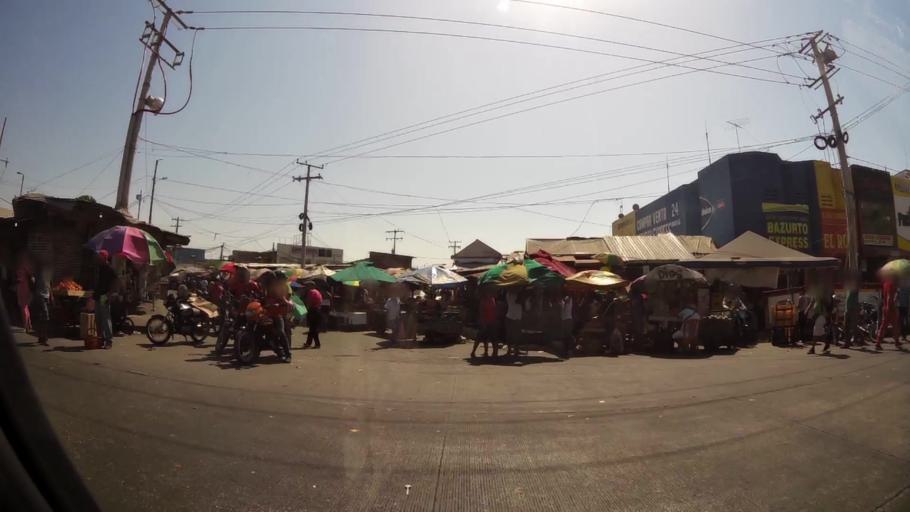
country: CO
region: Bolivar
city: Cartagena
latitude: 10.4129
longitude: -75.5229
